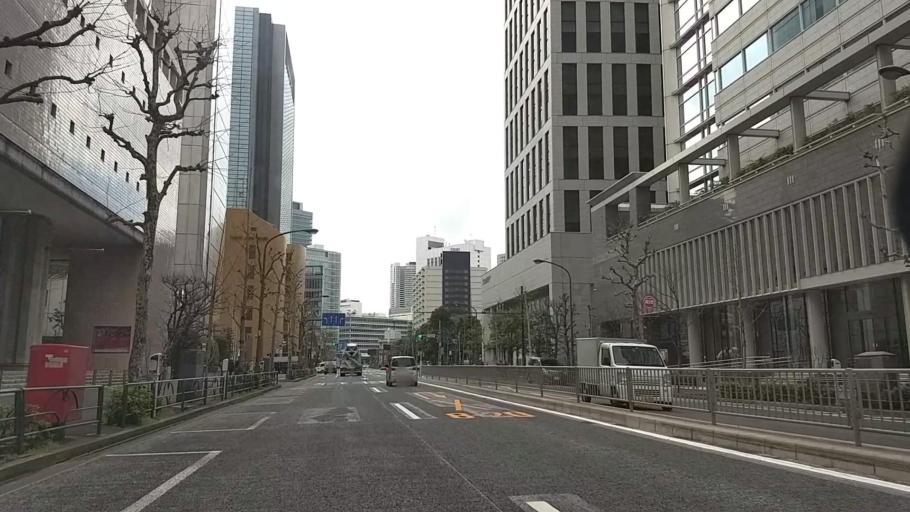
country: JP
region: Tokyo
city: Tokyo
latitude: 35.6513
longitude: 139.7495
